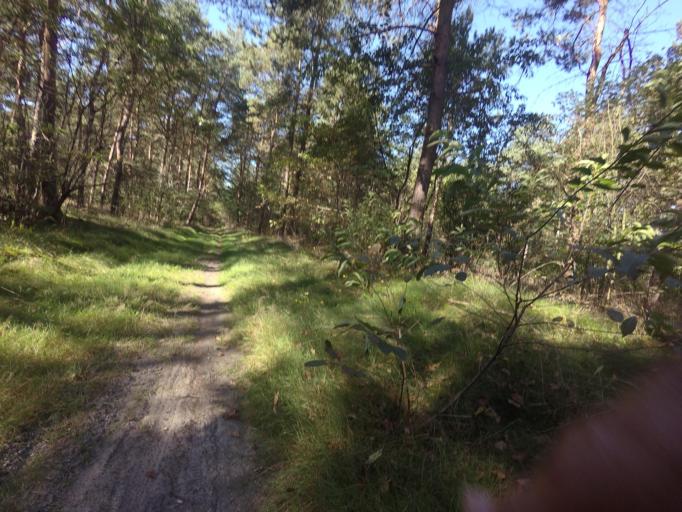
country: DE
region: Lower Saxony
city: Wielen
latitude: 52.5307
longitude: 6.7088
